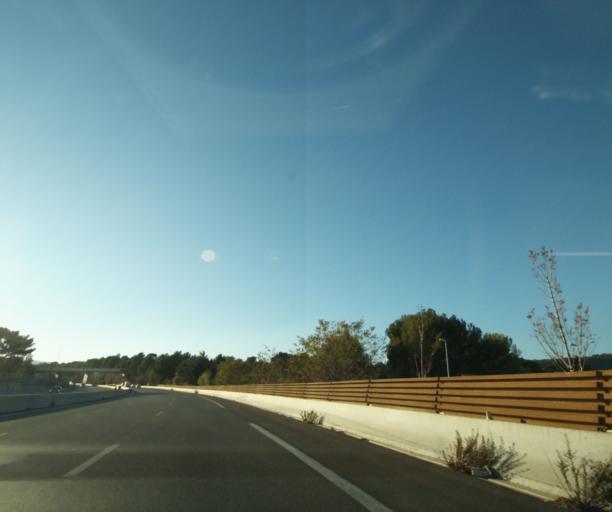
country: FR
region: Provence-Alpes-Cote d'Azur
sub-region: Departement des Bouches-du-Rhone
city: Ceyreste
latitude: 43.2100
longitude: 5.6250
